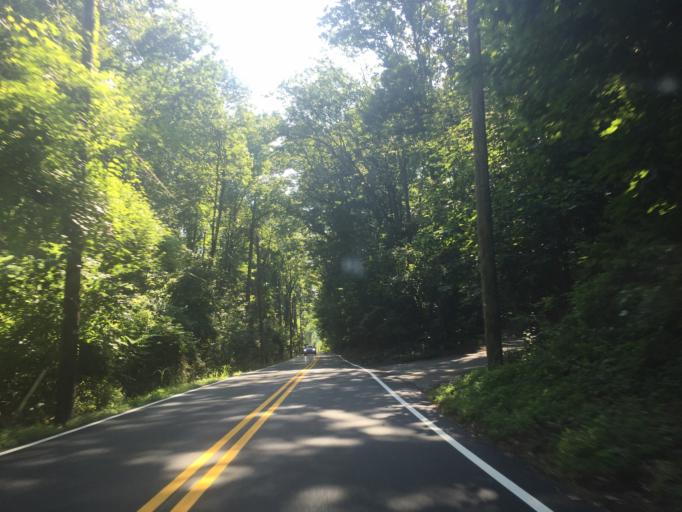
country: US
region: Maryland
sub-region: Baltimore County
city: Pikesville
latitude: 39.4121
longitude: -76.7007
